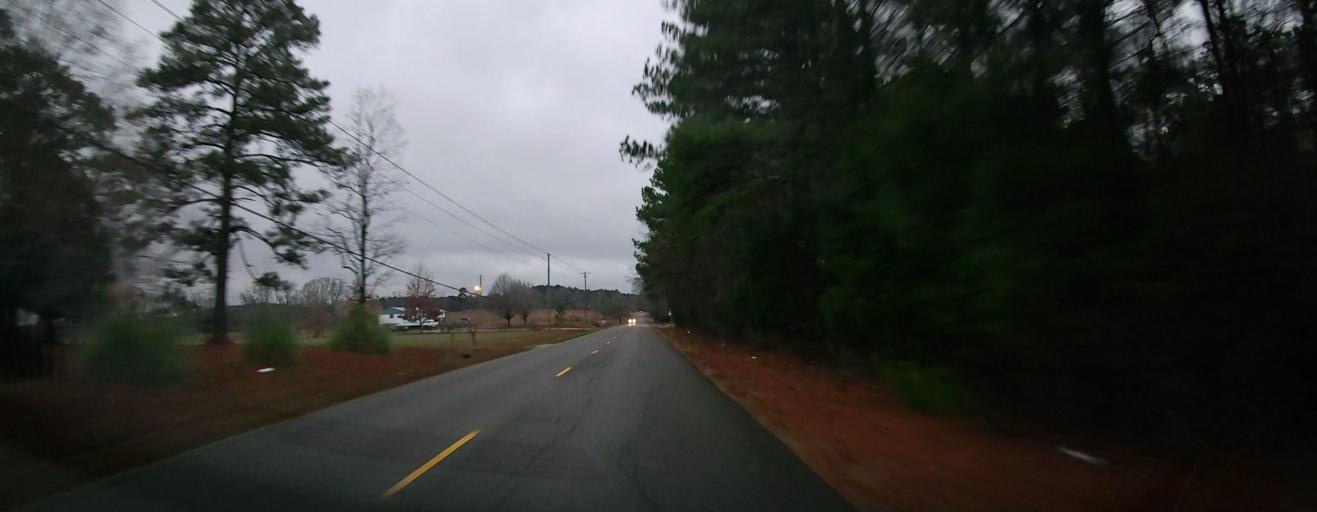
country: US
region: Alabama
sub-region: Tuscaloosa County
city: Vance
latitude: 33.1516
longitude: -87.2299
